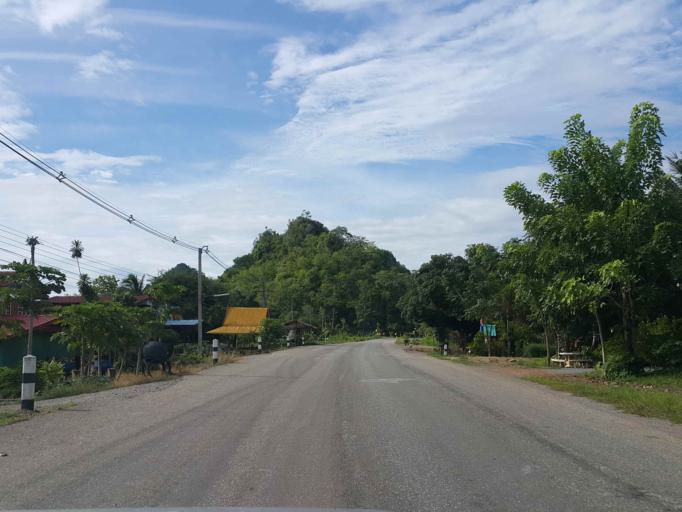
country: TH
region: Sukhothai
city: Thung Saliam
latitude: 17.2671
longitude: 99.5346
